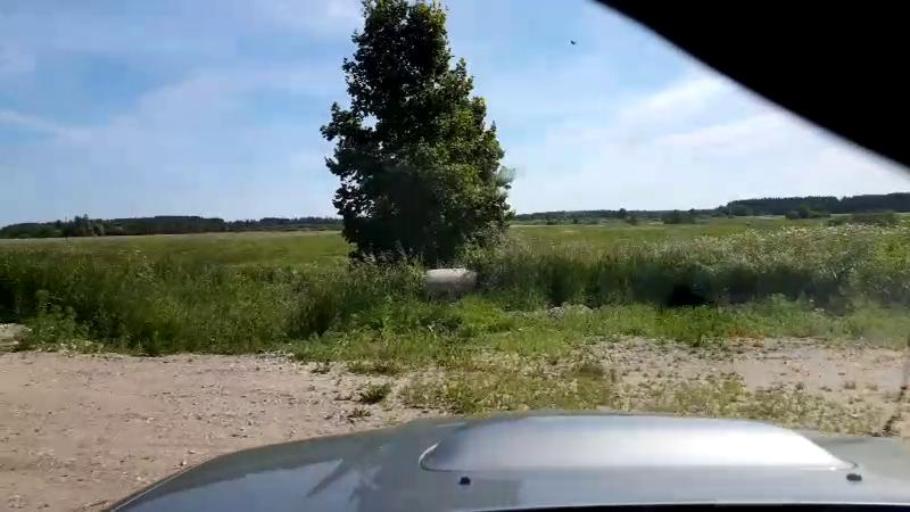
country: EE
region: Paernumaa
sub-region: Sauga vald
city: Sauga
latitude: 58.4760
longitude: 24.5351
